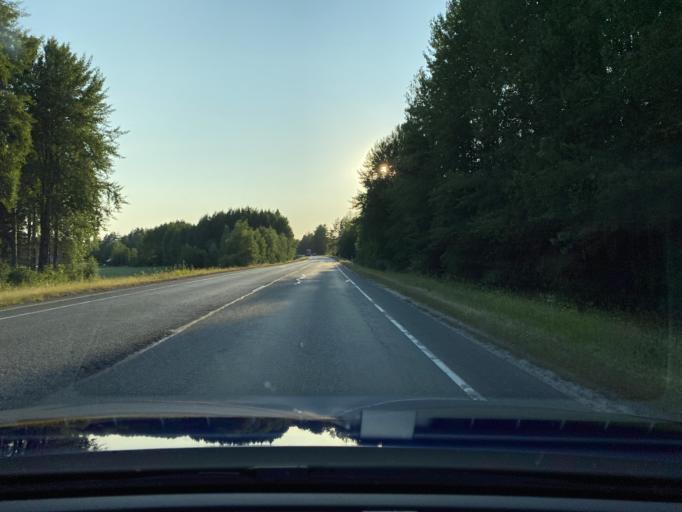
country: FI
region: Haeme
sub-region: Forssa
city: Tammela
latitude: 60.8277
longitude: 23.7368
